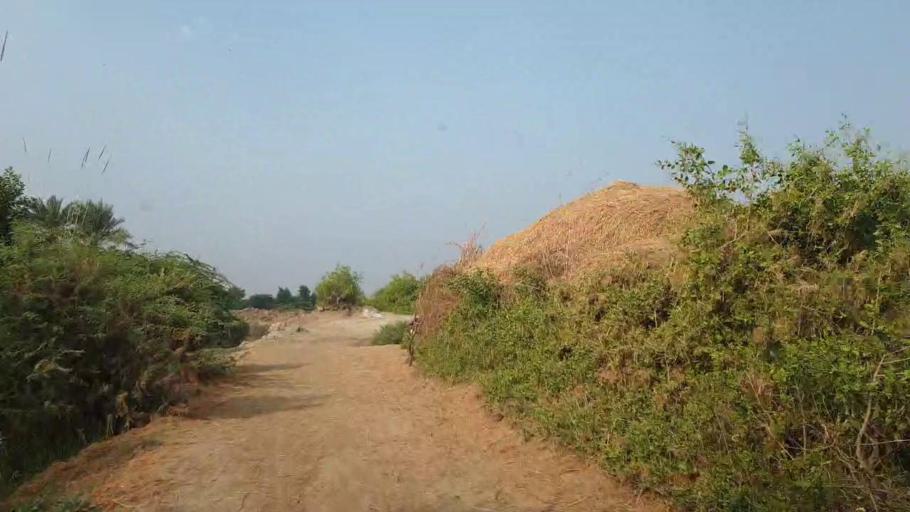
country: PK
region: Sindh
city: Talhar
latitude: 24.8420
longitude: 68.7983
